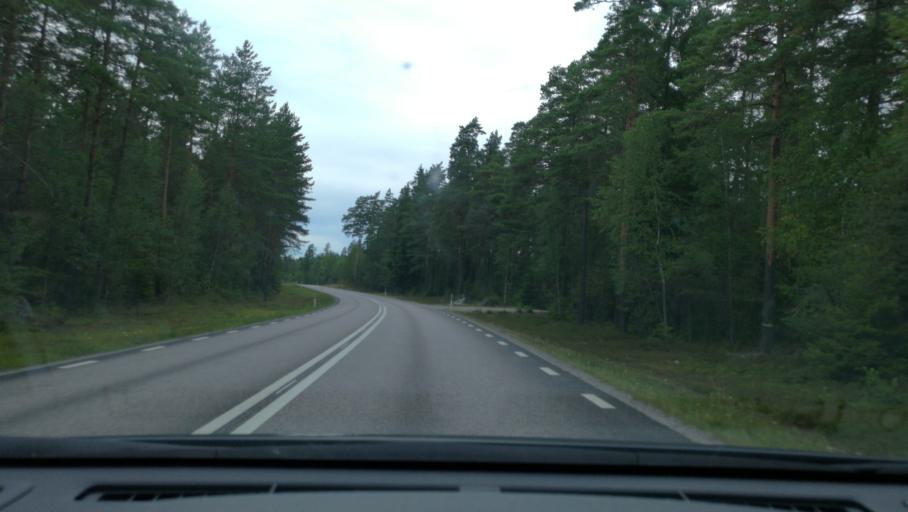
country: SE
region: Soedermanland
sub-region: Katrineholms Kommun
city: Katrineholm
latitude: 59.1098
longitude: 16.1758
